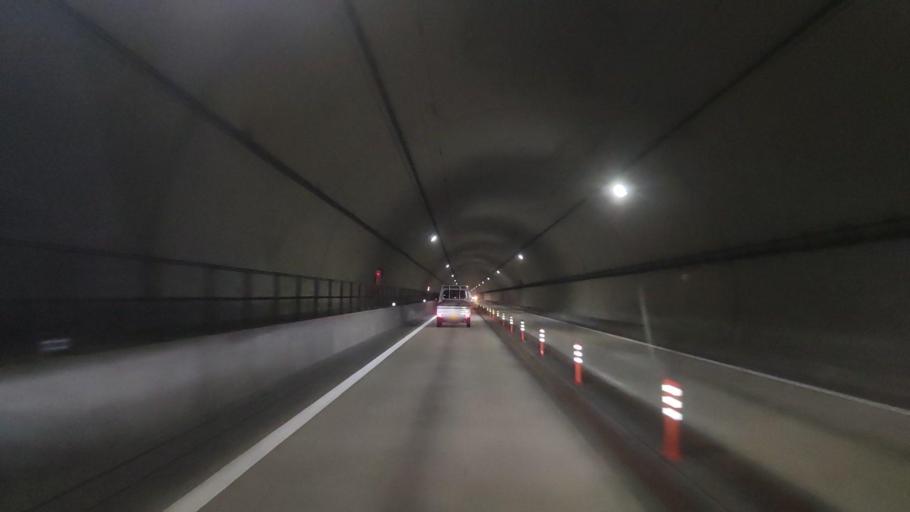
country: JP
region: Wakayama
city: Tanabe
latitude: 33.6061
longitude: 135.4288
